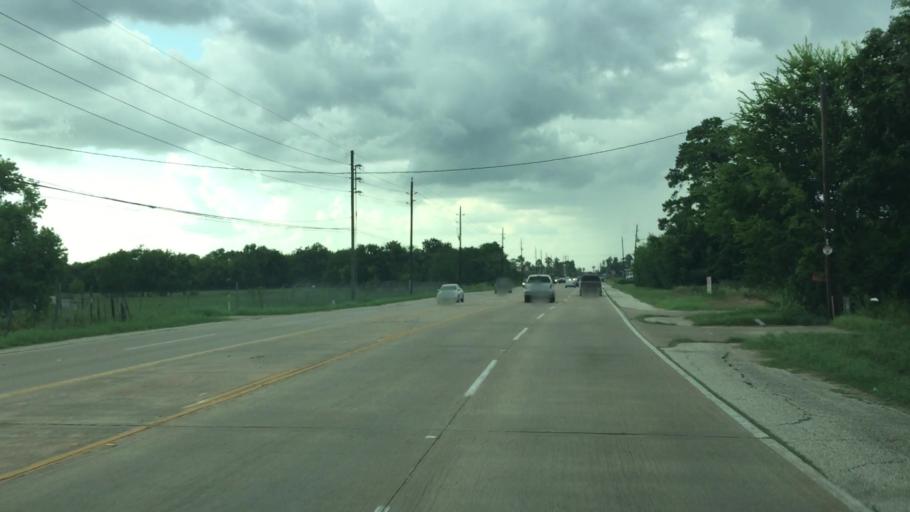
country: US
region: Texas
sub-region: Harris County
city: Hudson
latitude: 29.9938
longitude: -95.5027
